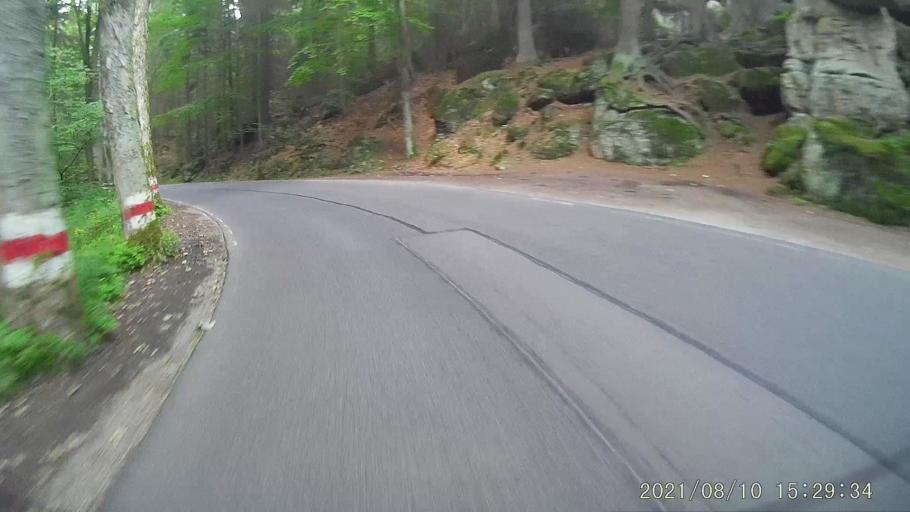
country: PL
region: Lower Silesian Voivodeship
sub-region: Powiat klodzki
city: Radkow
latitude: 50.4749
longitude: 16.3928
